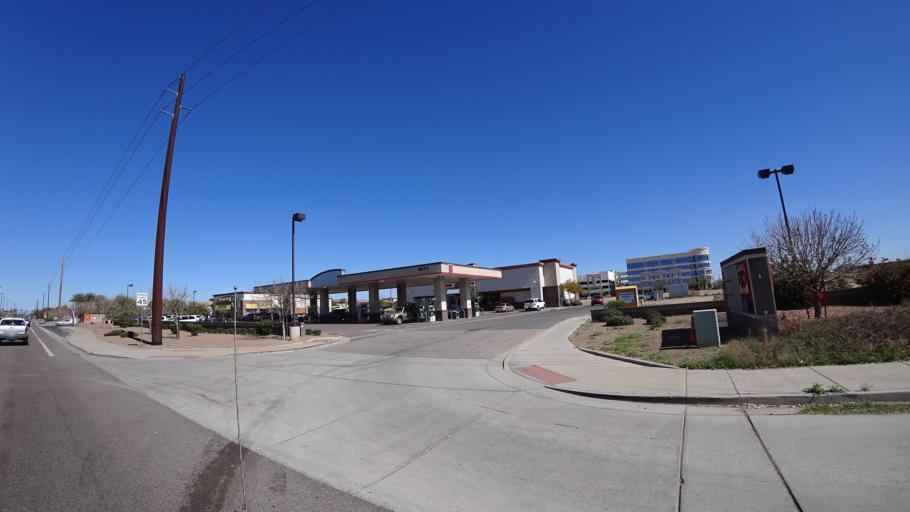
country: US
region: Arizona
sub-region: Maricopa County
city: Gilbert
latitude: 33.2963
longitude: -111.7554
